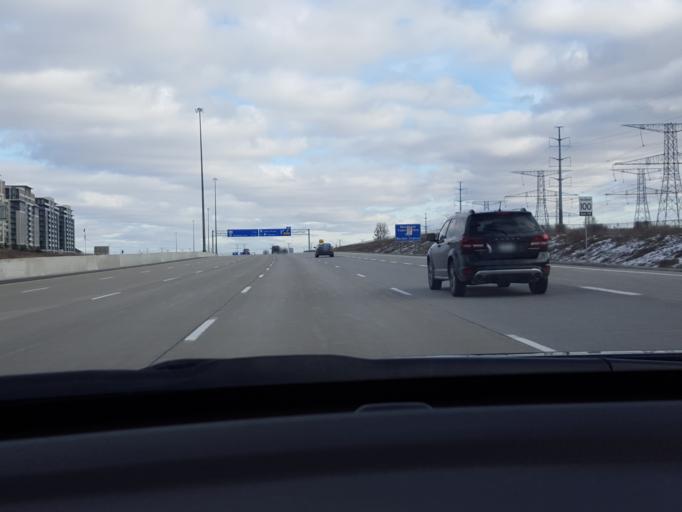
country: CA
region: Ontario
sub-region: York
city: Richmond Hill
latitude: 43.8369
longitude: -79.3966
